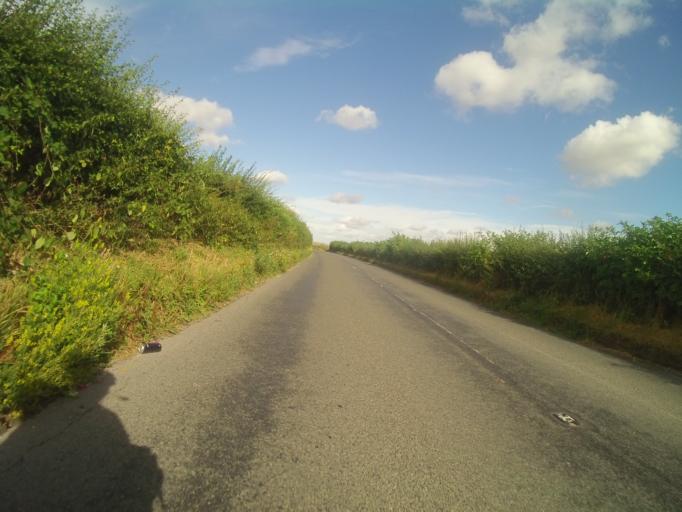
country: GB
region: England
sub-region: Wiltshire
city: Bulford
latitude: 51.1863
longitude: -1.7468
